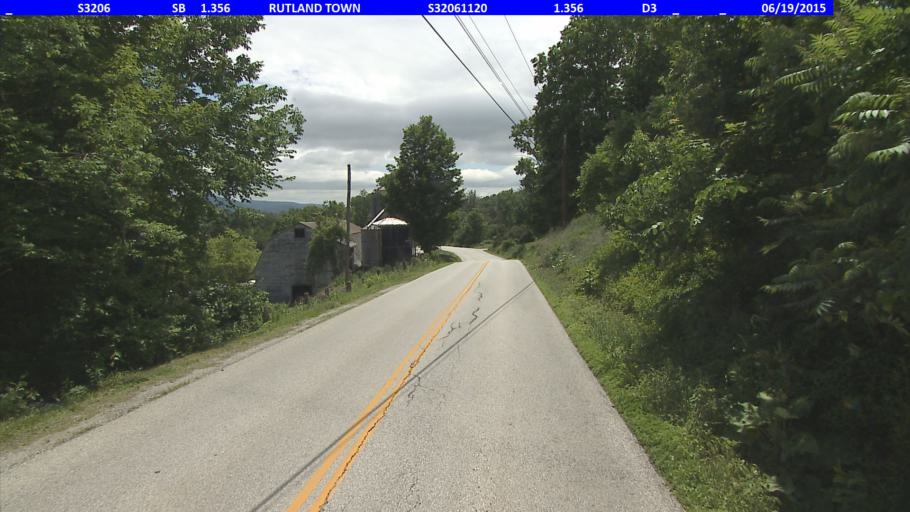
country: US
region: Vermont
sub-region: Rutland County
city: Rutland
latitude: 43.6482
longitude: -72.9961
